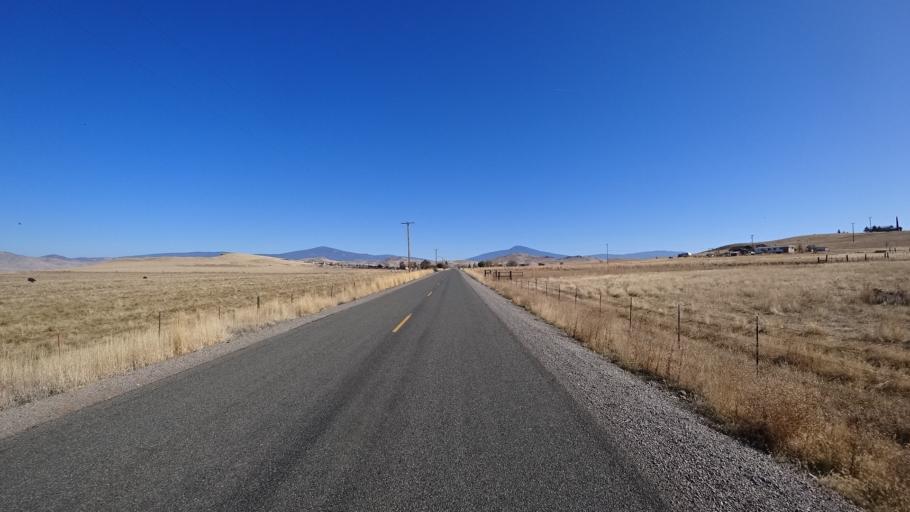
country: US
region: California
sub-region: Siskiyou County
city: Montague
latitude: 41.7558
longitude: -122.4712
